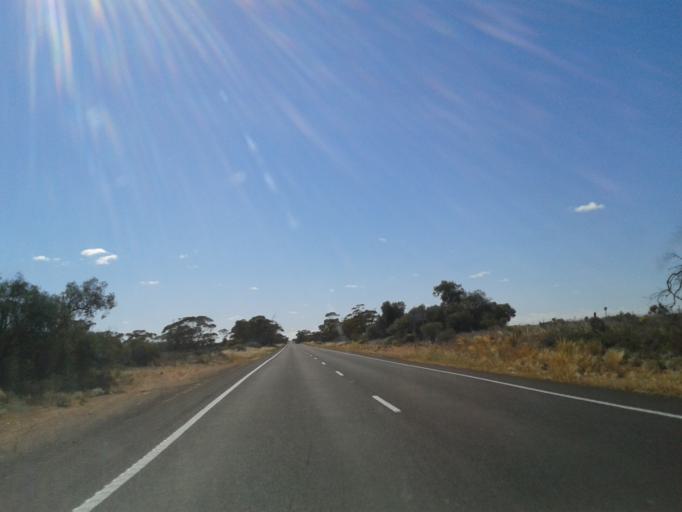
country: AU
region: South Australia
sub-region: Renmark Paringa
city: Renmark
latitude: -34.2746
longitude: 141.2344
